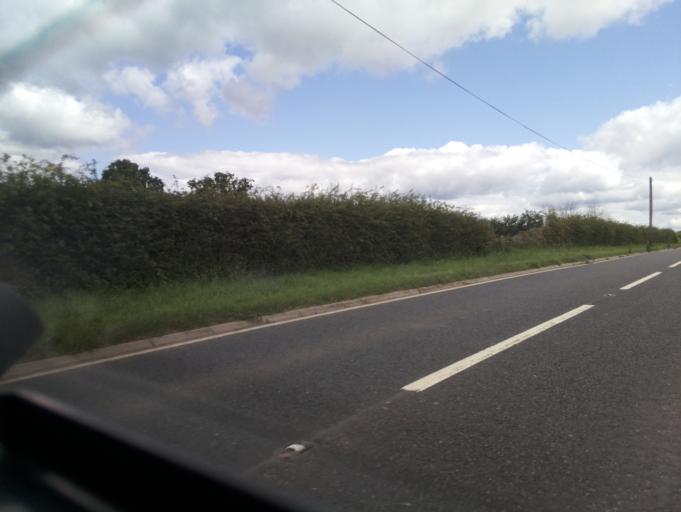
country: GB
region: Wales
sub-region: Monmouthshire
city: Chepstow
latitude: 51.6654
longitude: -2.6325
